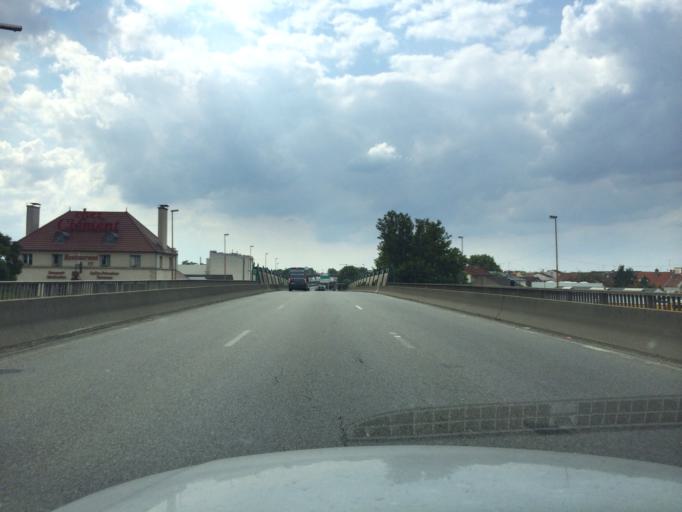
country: FR
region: Ile-de-France
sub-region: Departement de l'Essonne
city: Bievres
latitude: 48.7768
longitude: 2.2309
